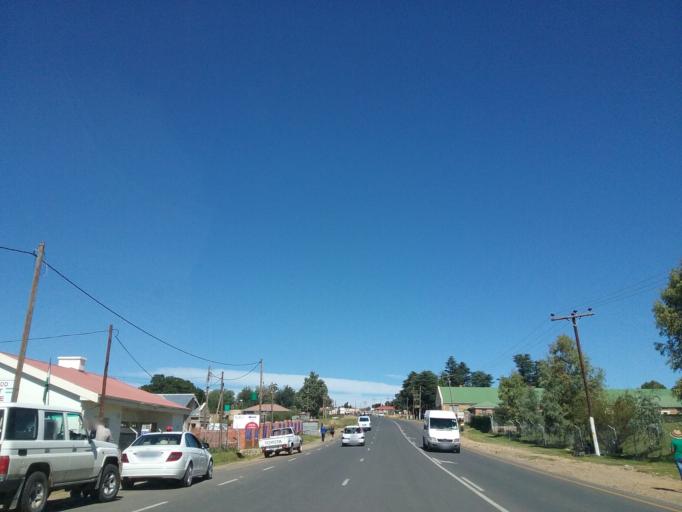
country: LS
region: Maseru
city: Maseru
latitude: -29.4148
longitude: 27.5589
